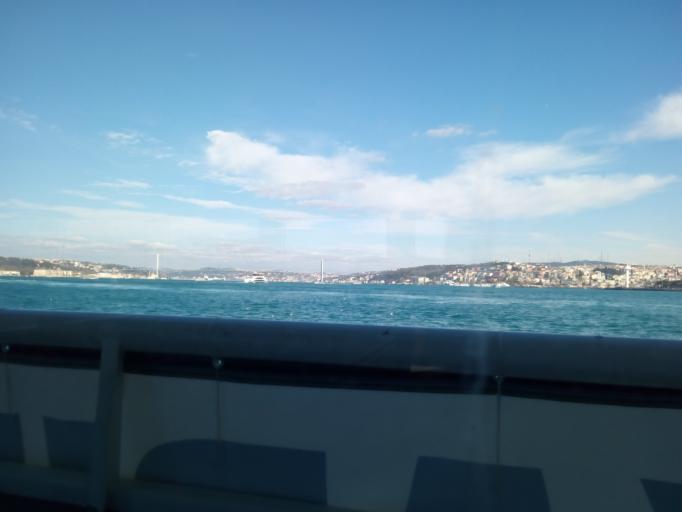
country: TR
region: Istanbul
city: Eminoenue
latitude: 41.0262
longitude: 28.9979
